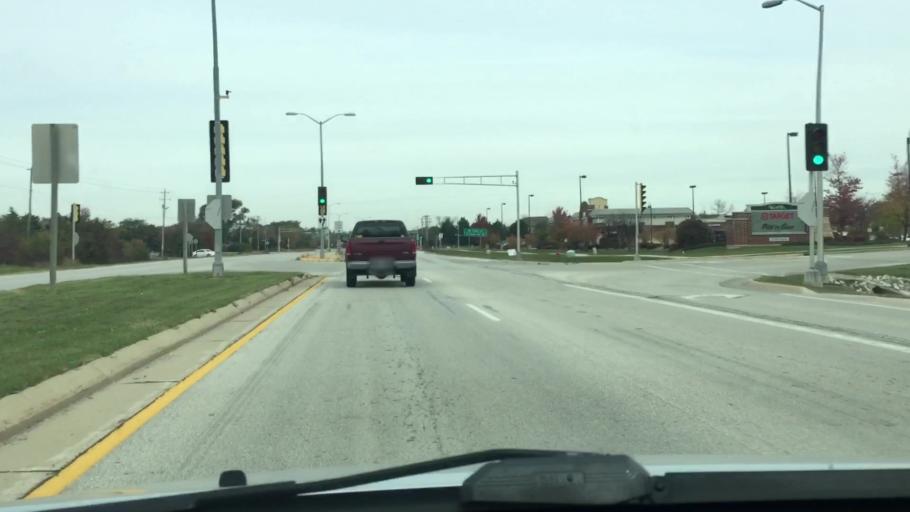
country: US
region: Wisconsin
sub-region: Milwaukee County
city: Franklin
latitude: 42.9034
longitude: -88.0391
